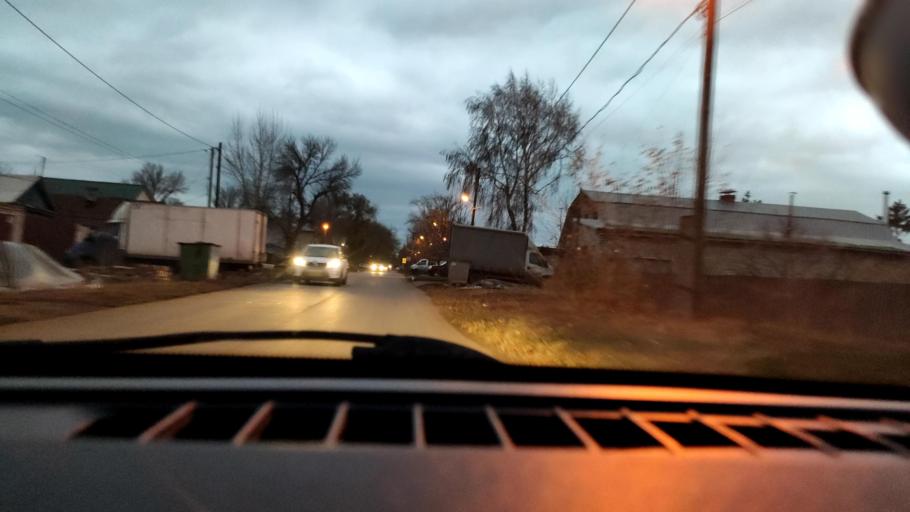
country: RU
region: Samara
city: Petra-Dubrava
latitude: 53.2511
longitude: 50.3285
